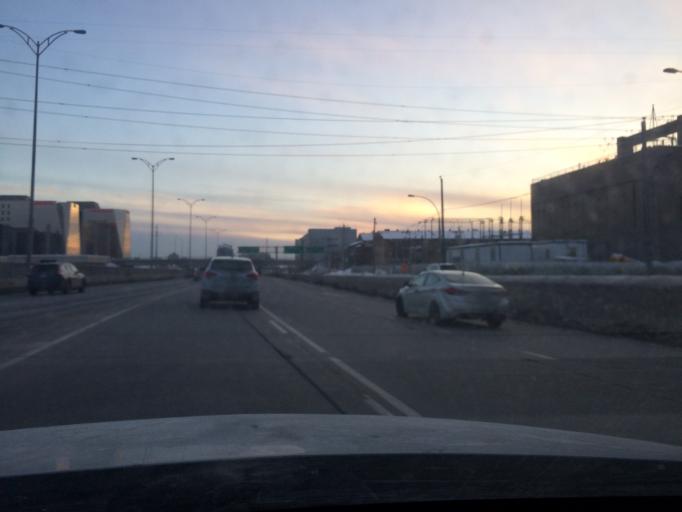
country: CA
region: Quebec
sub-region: Montreal
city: Saint-Leonard
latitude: 45.6022
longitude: -73.5690
